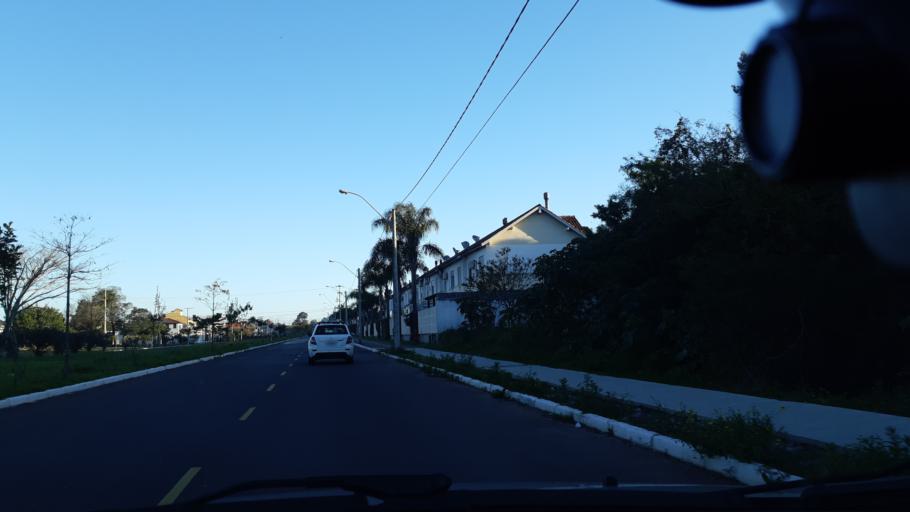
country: BR
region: Rio Grande do Sul
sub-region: Canoas
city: Canoas
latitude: -29.9199
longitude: -51.1553
